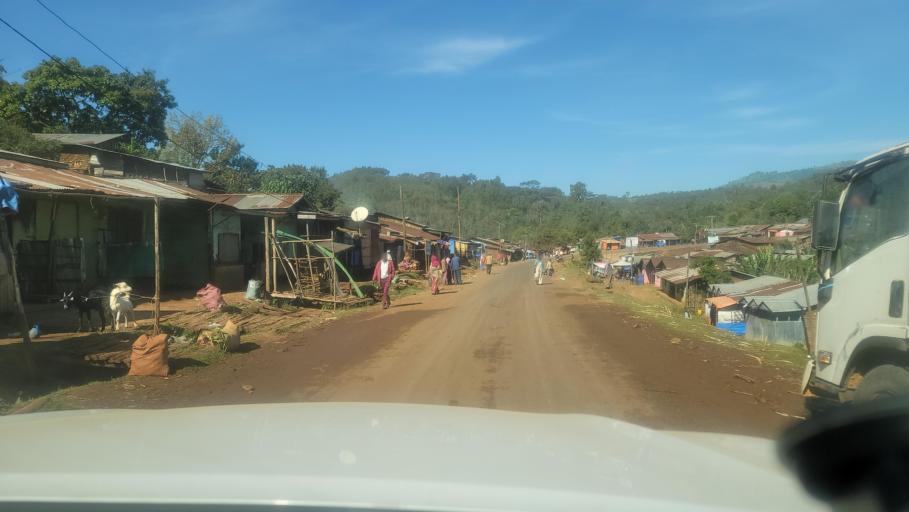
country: ET
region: Oromiya
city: Agaro
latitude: 7.7951
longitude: 36.4788
